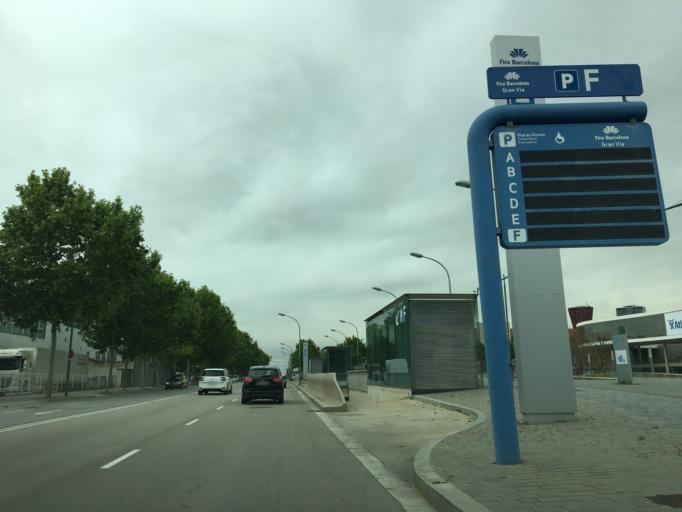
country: ES
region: Catalonia
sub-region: Provincia de Barcelona
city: Sants-Montjuic
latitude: 41.3549
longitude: 2.1384
